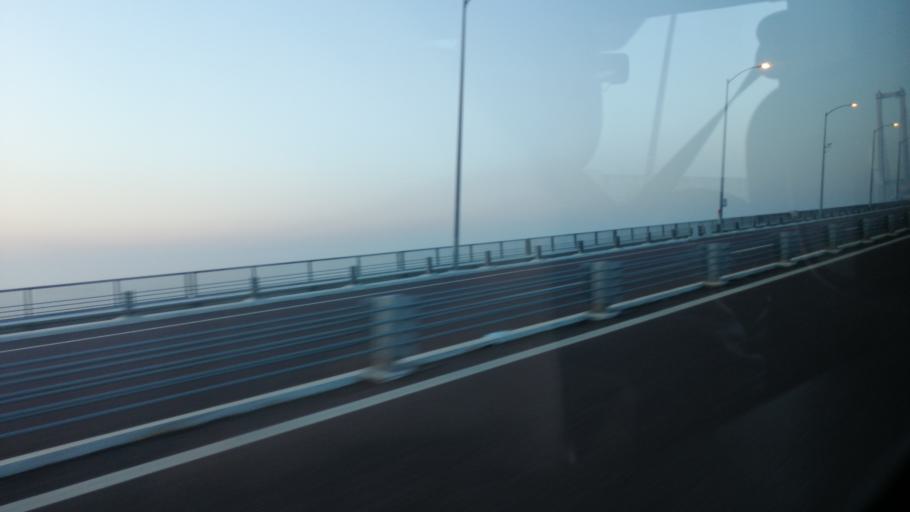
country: TR
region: Yalova
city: Altinova
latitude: 40.7365
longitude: 29.5124
